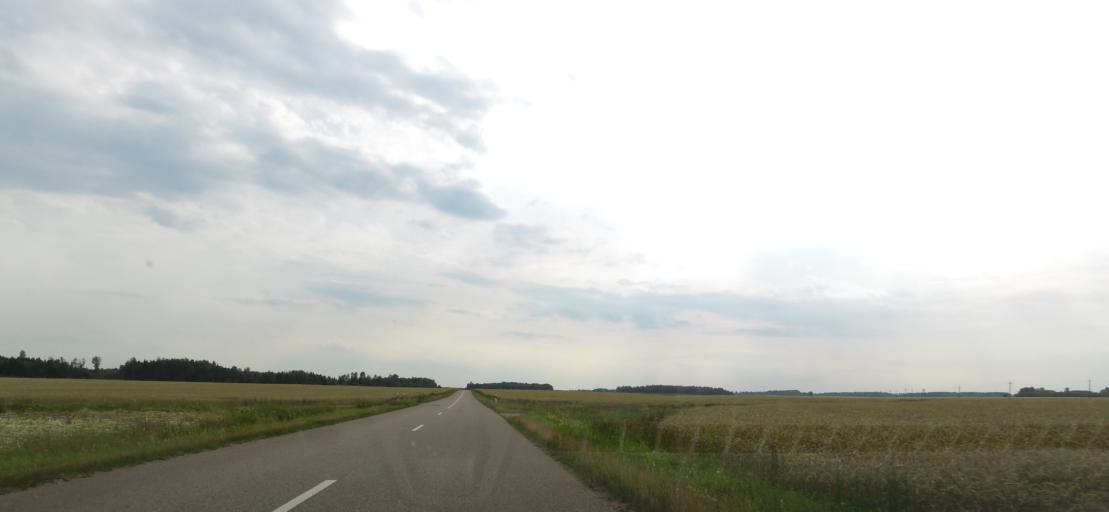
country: LT
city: Obeliai
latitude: 56.1183
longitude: 25.0927
